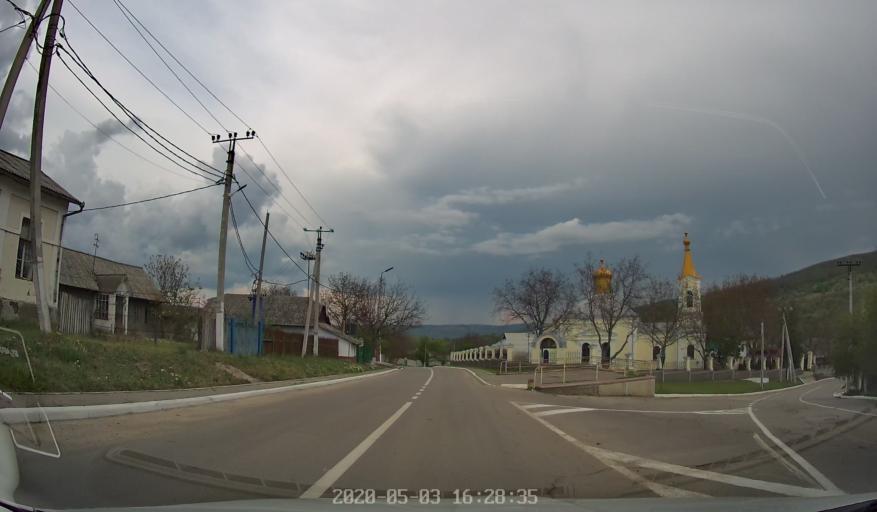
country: MD
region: Calarasi
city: Calarasi
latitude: 47.1925
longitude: 28.3523
